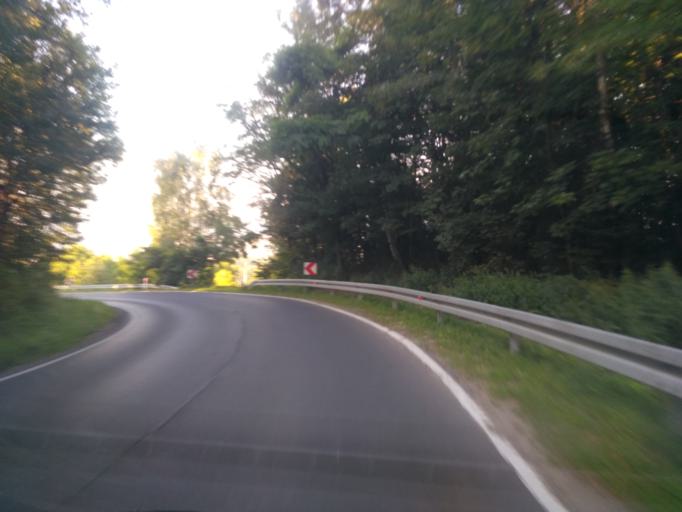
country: PL
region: Subcarpathian Voivodeship
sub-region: Powiat krosnienski
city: Korczyna
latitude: 49.7367
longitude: 21.8062
